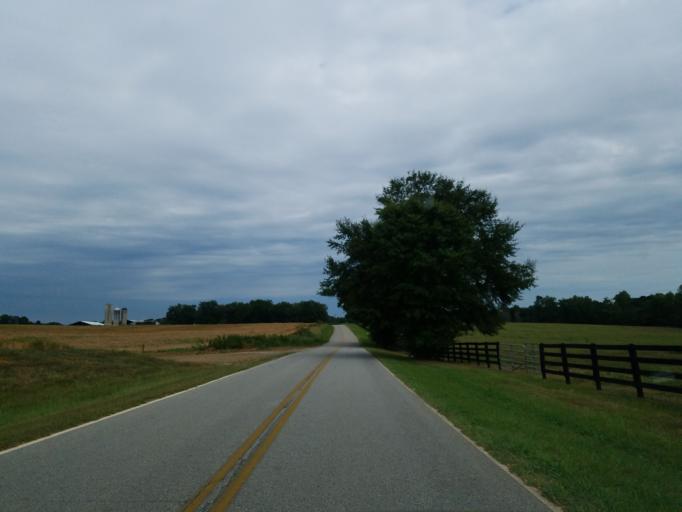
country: US
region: Georgia
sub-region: Lamar County
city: Barnesville
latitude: 33.0081
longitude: -84.0931
